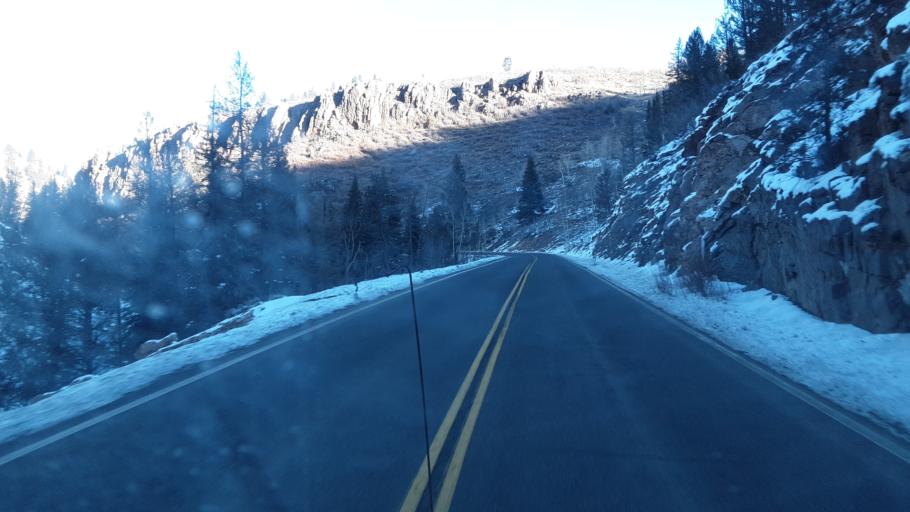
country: US
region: Colorado
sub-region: Hinsdale County
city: Lake City
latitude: 38.4101
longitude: -107.4059
